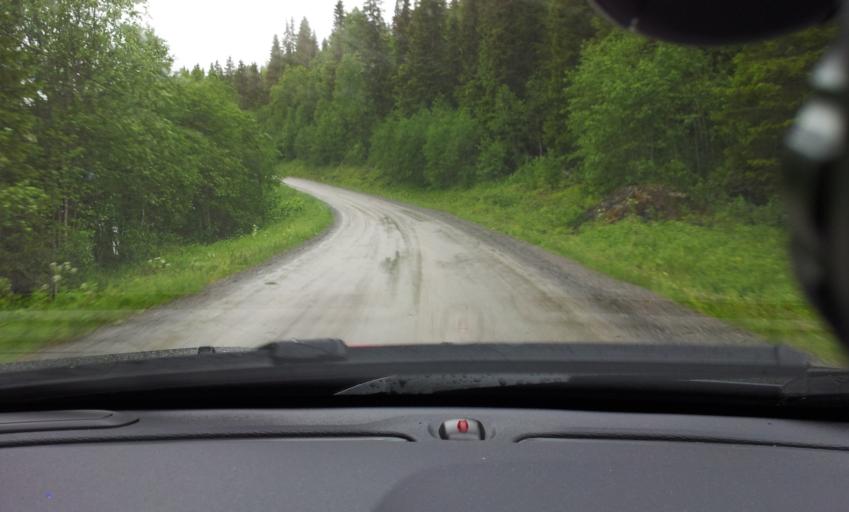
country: SE
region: Jaemtland
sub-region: Are Kommun
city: Are
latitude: 63.4994
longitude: 12.7581
